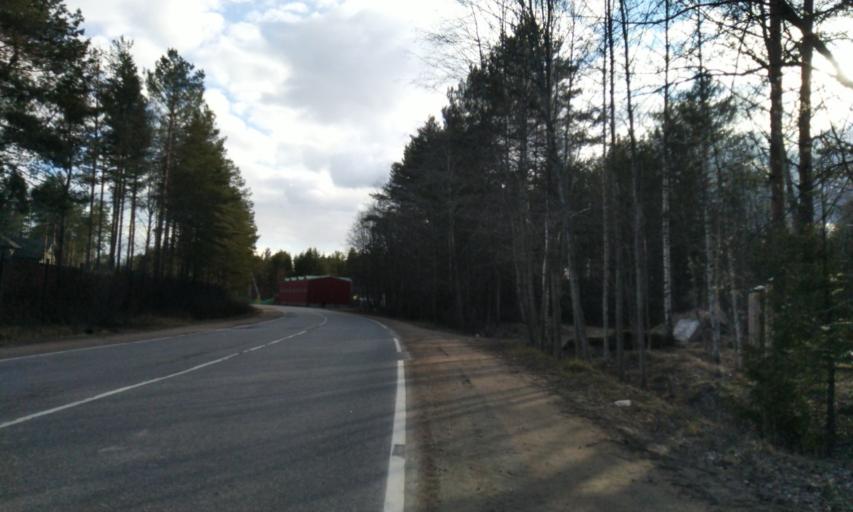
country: RU
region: Leningrad
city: Novoye Devyatkino
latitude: 60.1221
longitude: 30.4502
